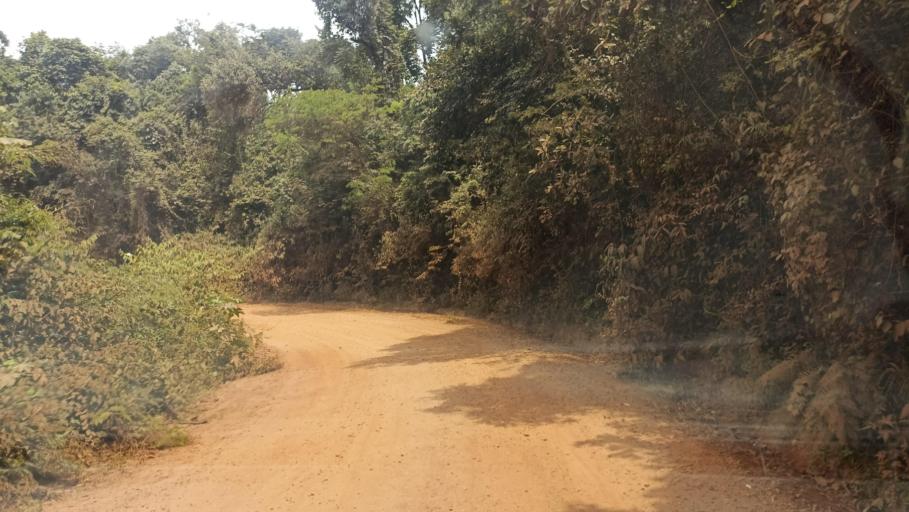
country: BR
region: Minas Gerais
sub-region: Itabirito
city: Itabirito
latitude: -20.3391
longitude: -43.7710
